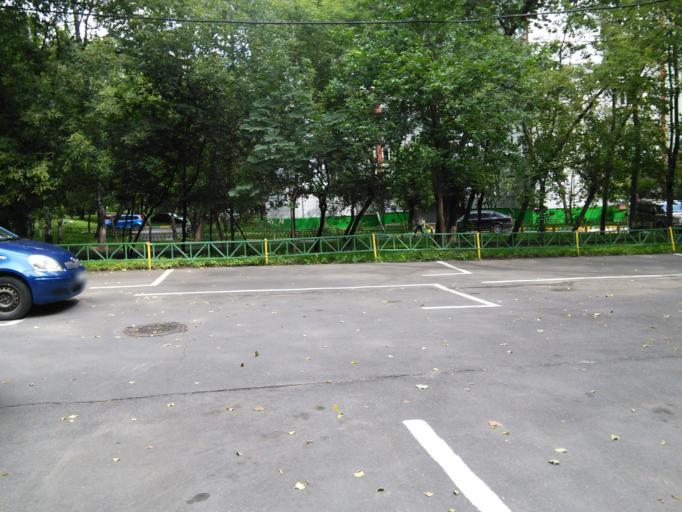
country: RU
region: Moskovskaya
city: Bogorodskoye
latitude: 55.7918
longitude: 37.7269
